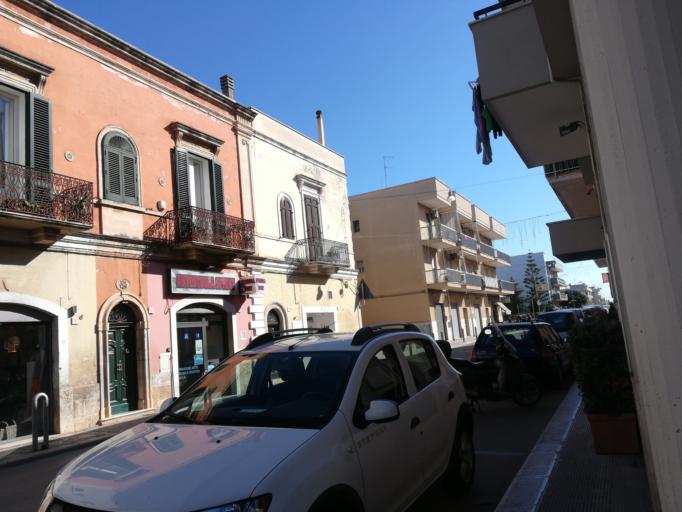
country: IT
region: Apulia
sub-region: Provincia di Bari
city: Polignano a Mare
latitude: 40.9920
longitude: 17.2252
